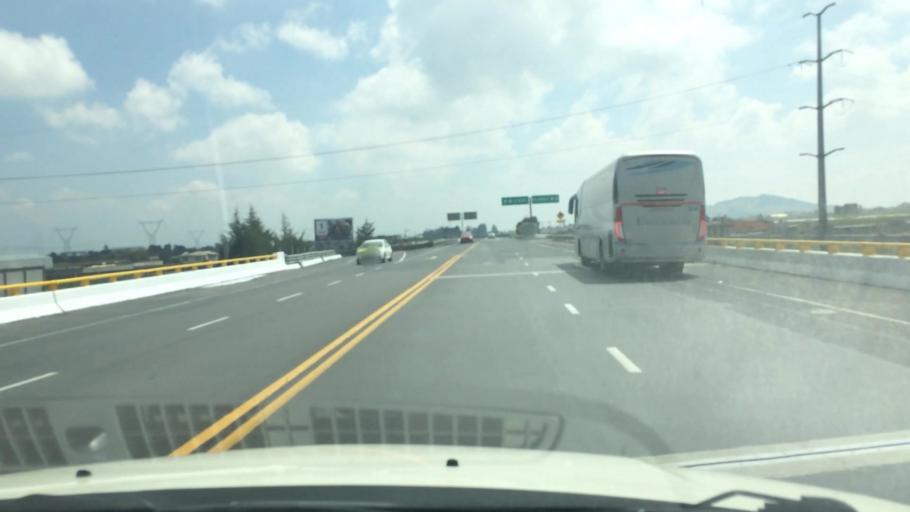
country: MX
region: Mexico
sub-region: Toluca
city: Colonia Aviacion Autopan
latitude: 19.3868
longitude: -99.7069
